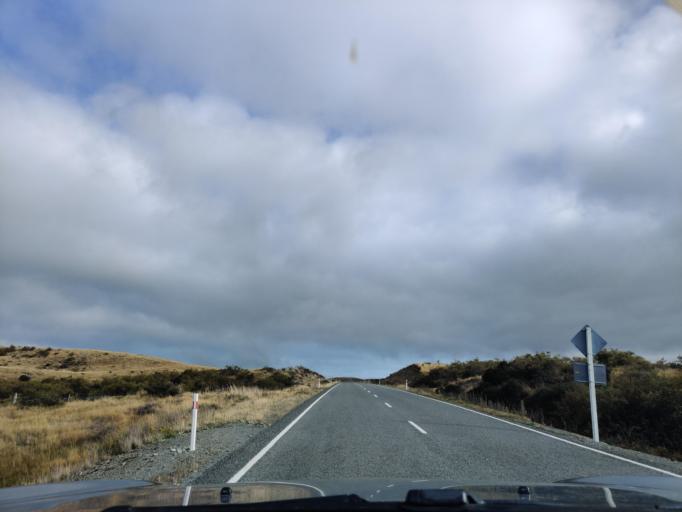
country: NZ
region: Canterbury
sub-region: Timaru District
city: Pleasant Point
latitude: -44.1951
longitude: 170.2440
